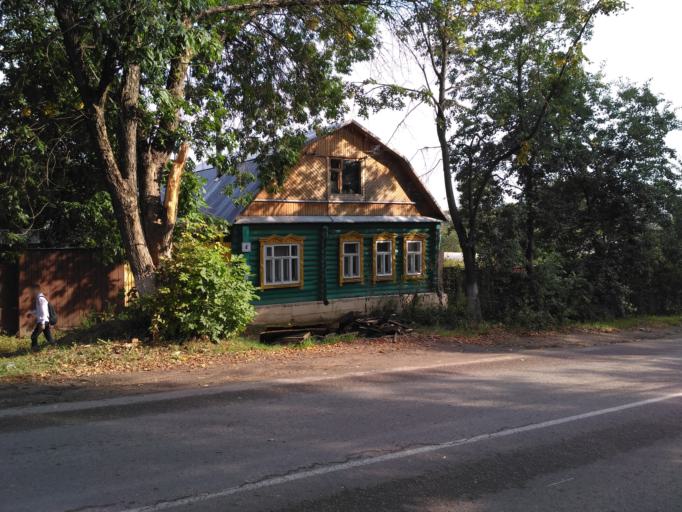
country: RU
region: Moskovskaya
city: Sergiyev Posad
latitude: 56.3092
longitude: 38.1242
